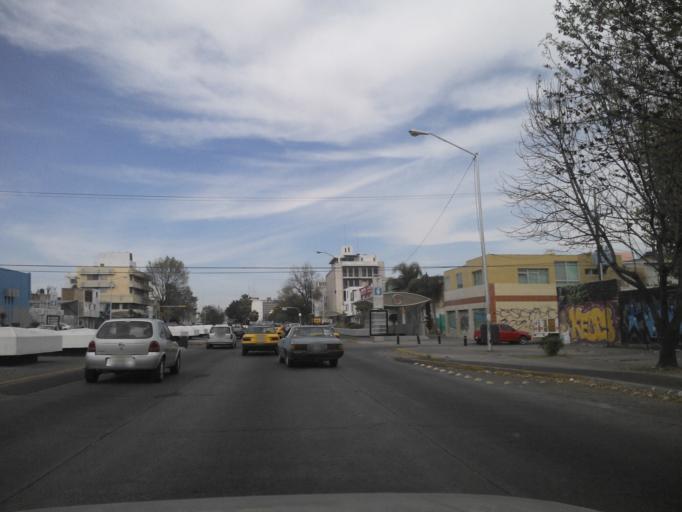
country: MX
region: Jalisco
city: Guadalajara
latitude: 20.6662
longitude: -103.3555
